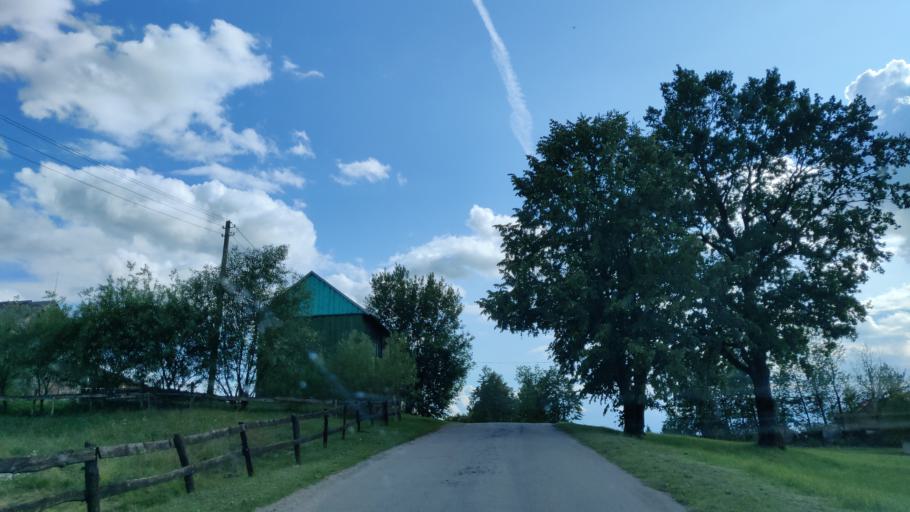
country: LT
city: Varniai
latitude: 55.5941
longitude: 22.3094
